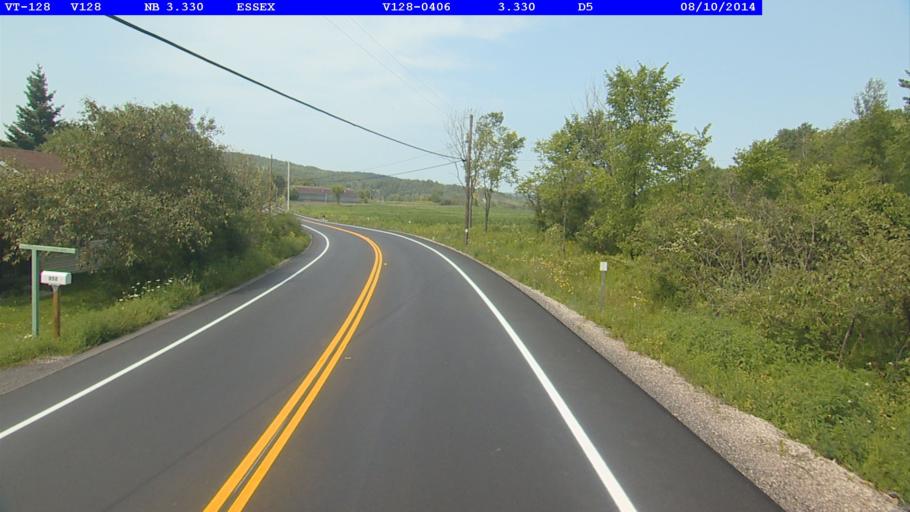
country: US
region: Vermont
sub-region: Chittenden County
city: Jericho
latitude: 44.5457
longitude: -73.0332
